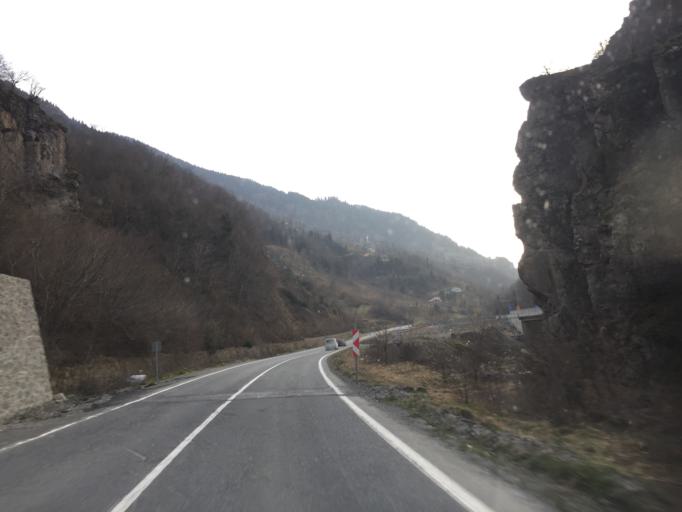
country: TR
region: Trabzon
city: Macka
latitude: 40.7484
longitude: 39.5623
